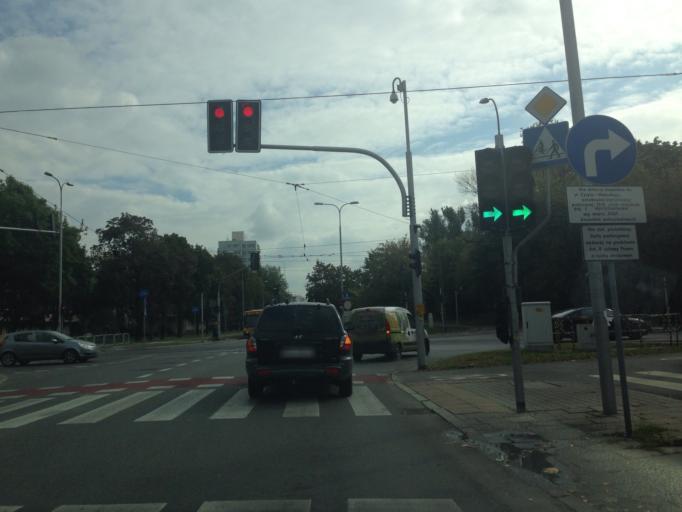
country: PL
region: Masovian Voivodeship
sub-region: Warszawa
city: Praga Polnoc
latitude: 52.2568
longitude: 21.0288
